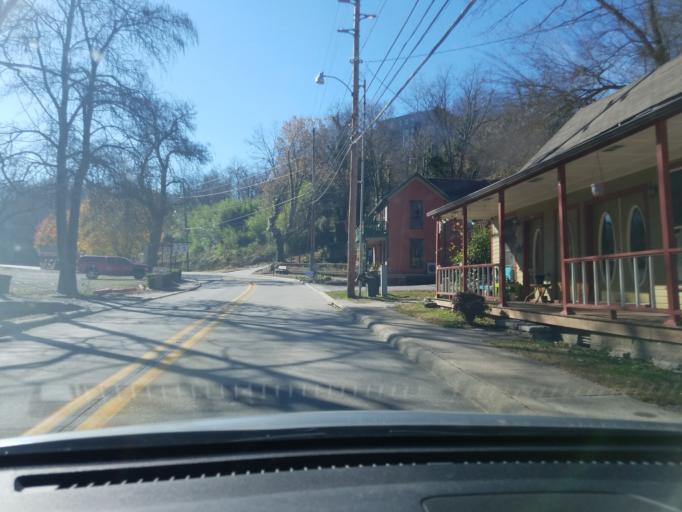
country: US
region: Arkansas
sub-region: Carroll County
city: Eureka Springs
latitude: 36.4046
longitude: -93.7357
